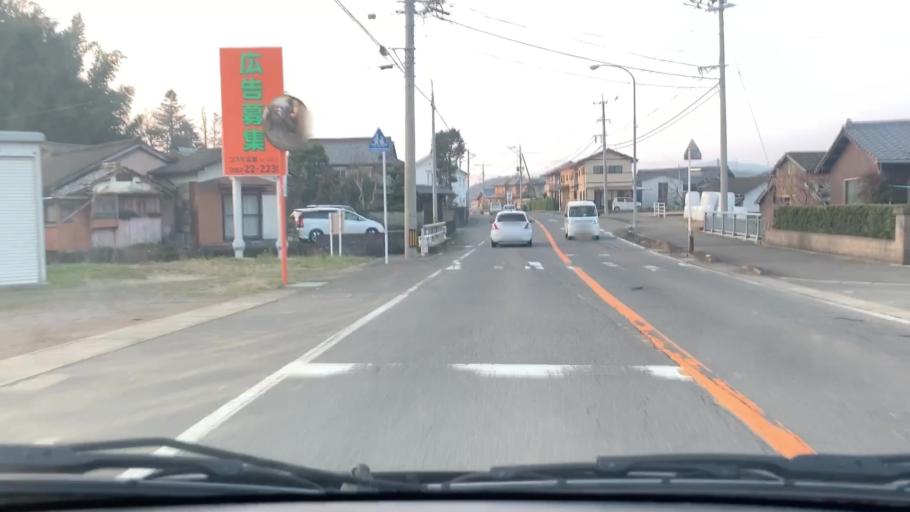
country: JP
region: Saga Prefecture
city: Imaricho-ko
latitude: 33.2668
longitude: 129.9011
